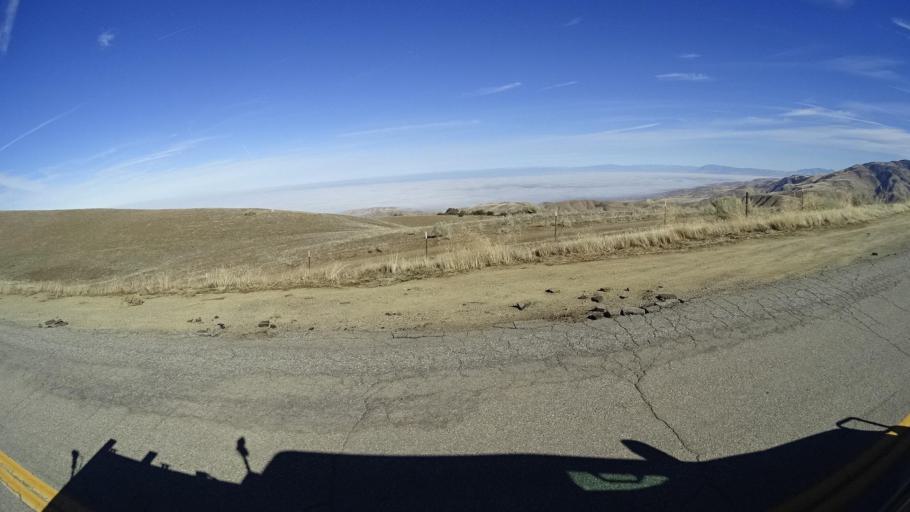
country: US
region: California
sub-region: Kern County
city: Maricopa
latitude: 34.9015
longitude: -119.3685
